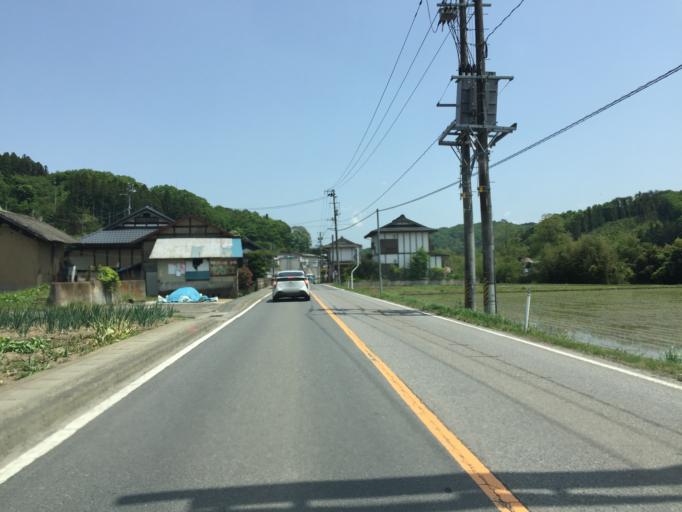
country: JP
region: Fukushima
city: Ishikawa
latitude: 37.1413
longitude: 140.4189
